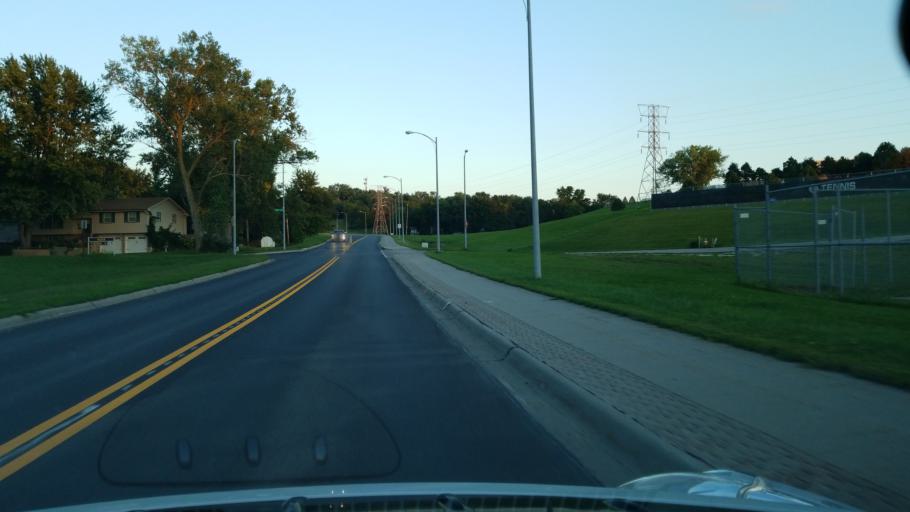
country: US
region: Nebraska
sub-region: Sarpy County
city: Bellevue
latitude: 41.1496
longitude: -95.9048
